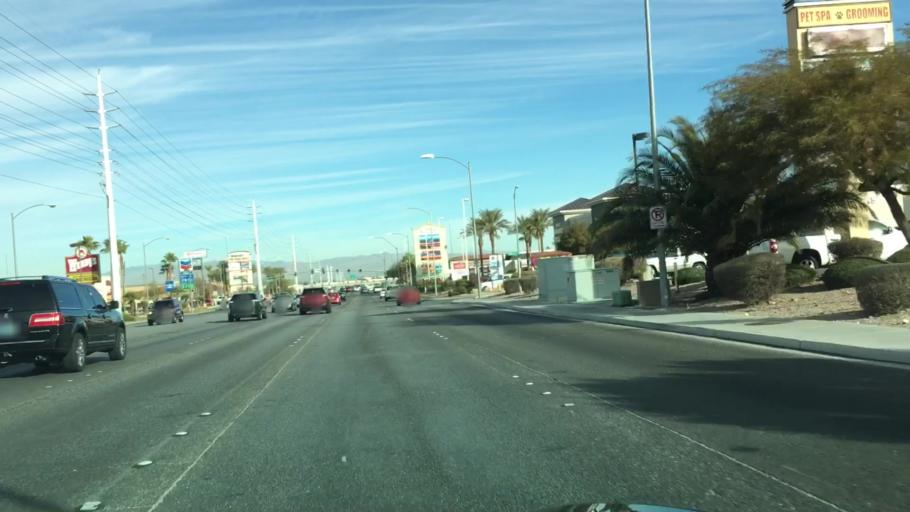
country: US
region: Nevada
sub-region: Clark County
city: Whitney
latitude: 36.0180
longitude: -115.1185
